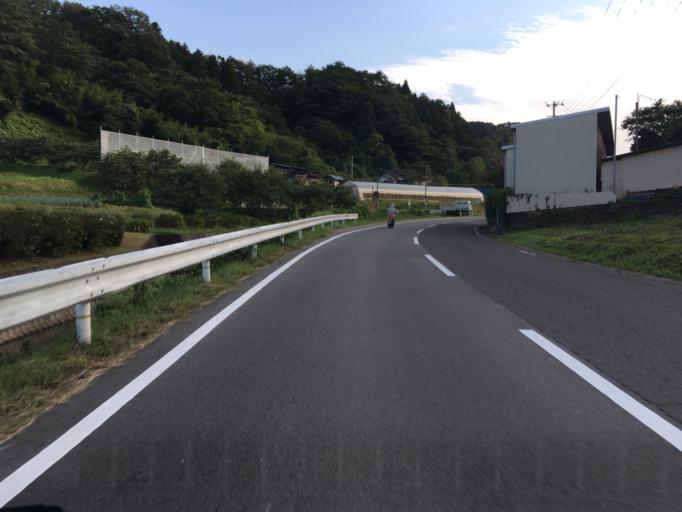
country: JP
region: Fukushima
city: Hobaramachi
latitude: 37.7152
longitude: 140.5895
